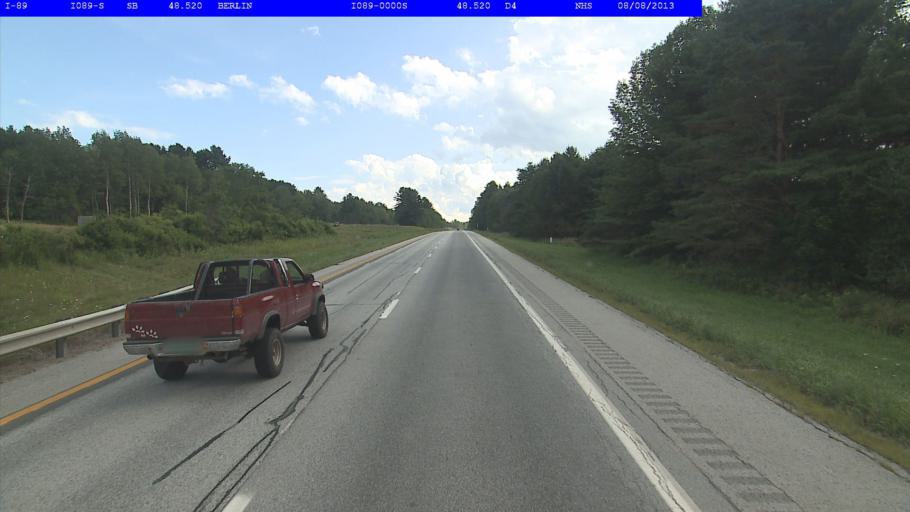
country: US
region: Vermont
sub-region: Washington County
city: Montpelier
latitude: 44.1908
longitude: -72.5770
